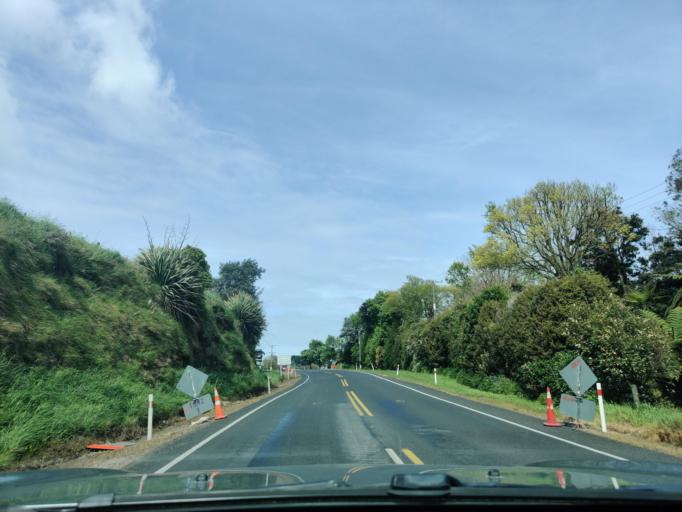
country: NZ
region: Taranaki
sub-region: South Taranaki District
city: Hawera
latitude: -39.5867
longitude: 174.2518
